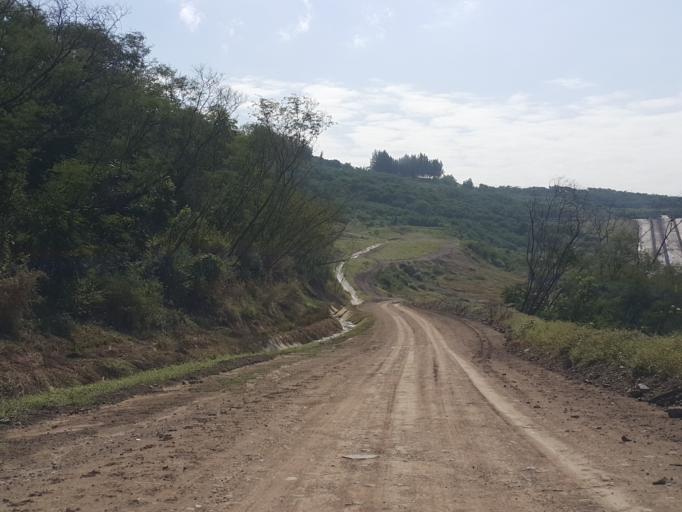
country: TH
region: Lampang
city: Mae Mo
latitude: 18.3258
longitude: 99.7374
